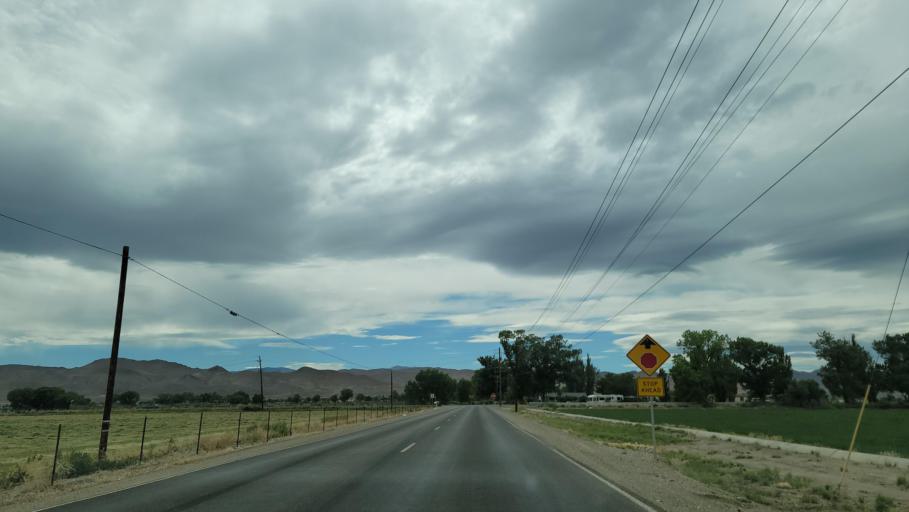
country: US
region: Nevada
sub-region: Lyon County
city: Yerington
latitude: 39.0481
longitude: -119.1791
